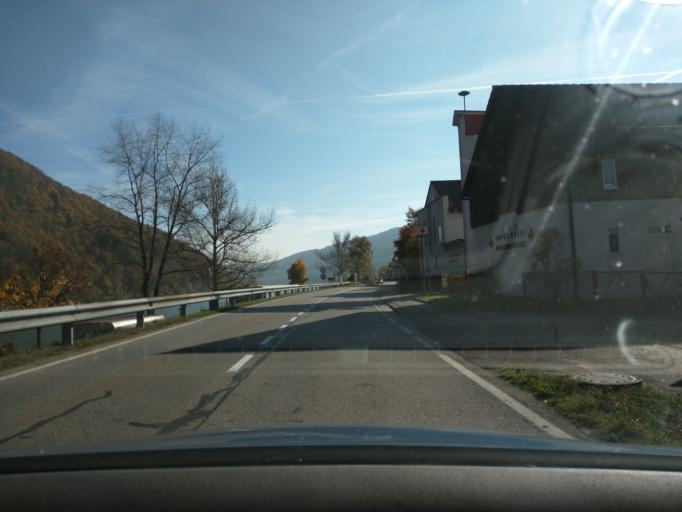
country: AT
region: Upper Austria
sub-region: Politischer Bezirk Rohrbach
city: Pfarrkirchen im Muehlkreis
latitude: 48.5061
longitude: 13.7335
